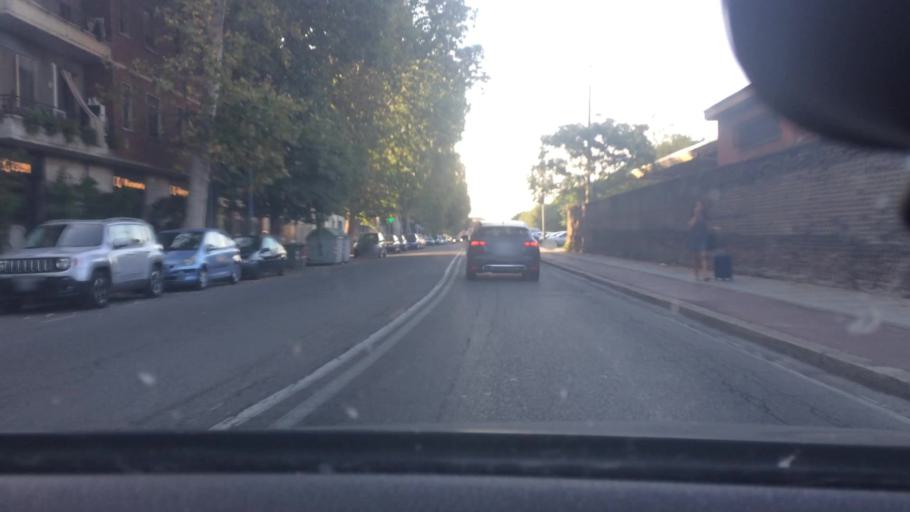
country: IT
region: Emilia-Romagna
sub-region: Provincia di Piacenza
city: Piacenza
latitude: 45.0523
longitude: 9.7048
